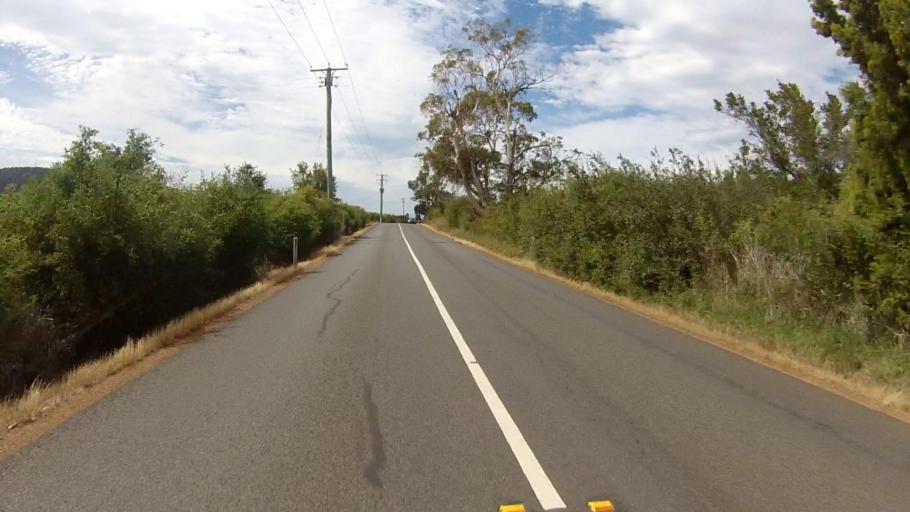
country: AU
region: Tasmania
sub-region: Brighton
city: Old Beach
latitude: -42.7048
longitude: 147.3664
